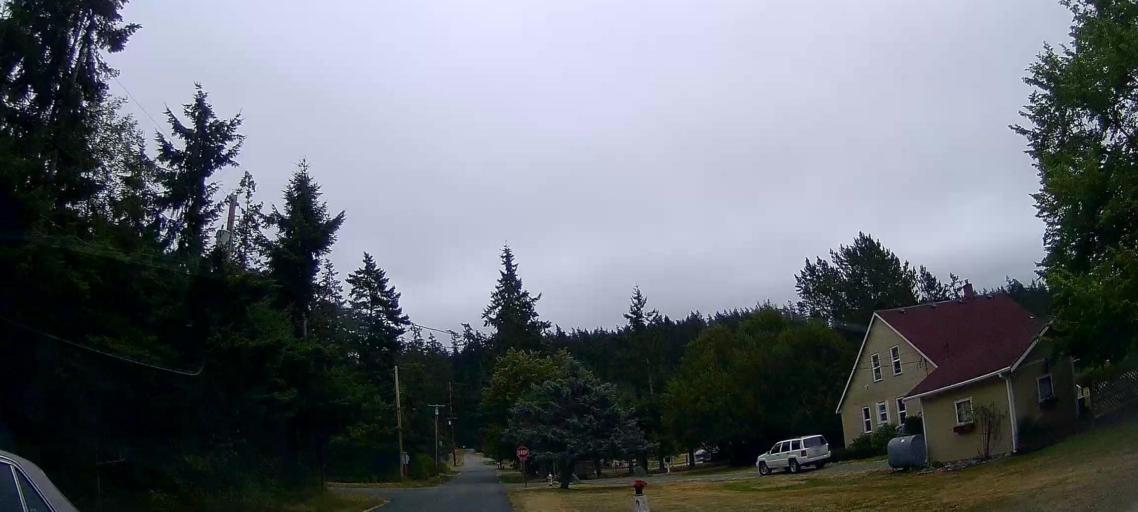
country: US
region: Washington
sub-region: Skagit County
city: Anacortes
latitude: 48.4335
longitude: -122.6095
